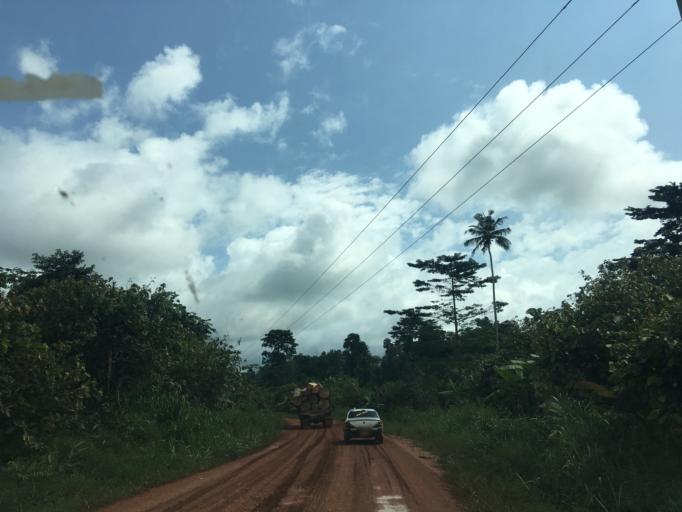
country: GH
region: Western
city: Wassa-Akropong
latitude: 5.7880
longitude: -2.3886
